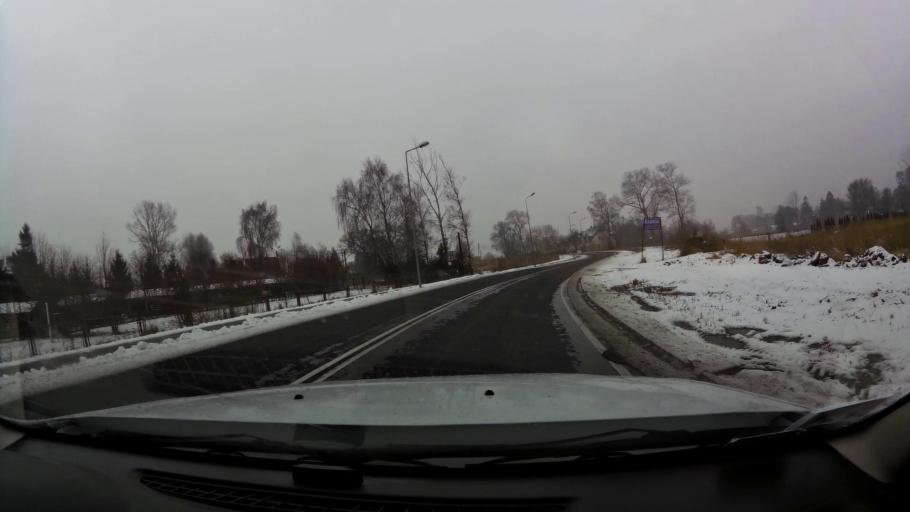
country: PL
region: West Pomeranian Voivodeship
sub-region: Powiat gryficki
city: Mrzezyno
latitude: 54.1366
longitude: 15.2853
